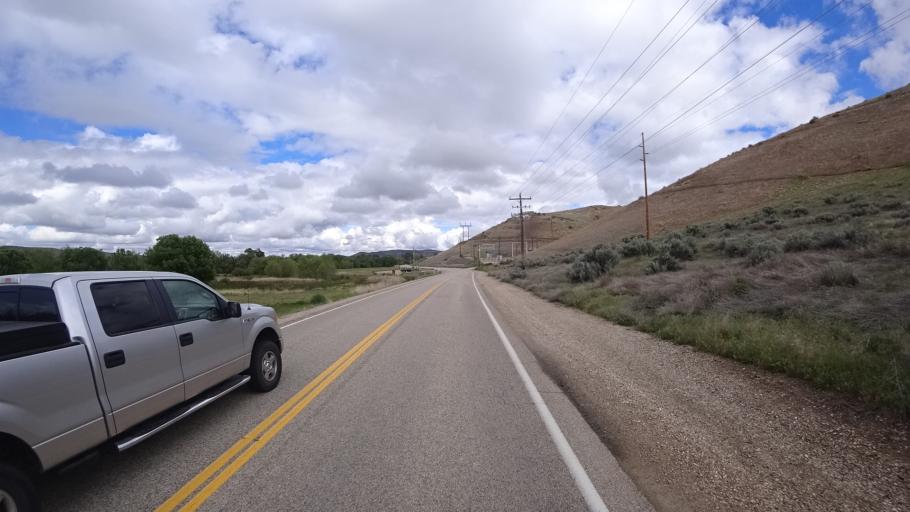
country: US
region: Idaho
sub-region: Ada County
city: Garden City
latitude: 43.7247
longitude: -116.2464
